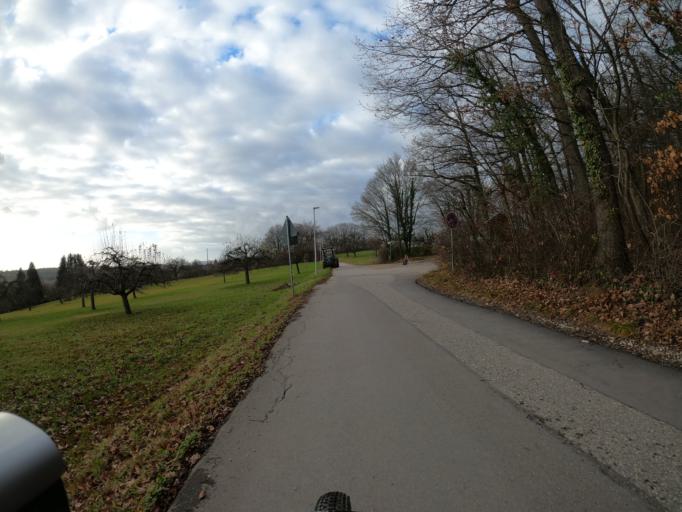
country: DE
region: Baden-Wuerttemberg
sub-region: Regierungsbezirk Stuttgart
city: Notzingen
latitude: 48.6763
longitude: 9.4558
